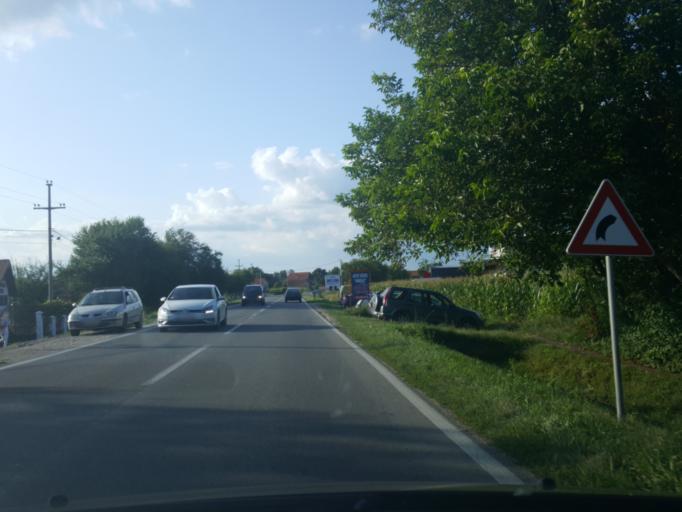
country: RS
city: Lipnicki Sor
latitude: 44.6001
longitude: 19.2549
